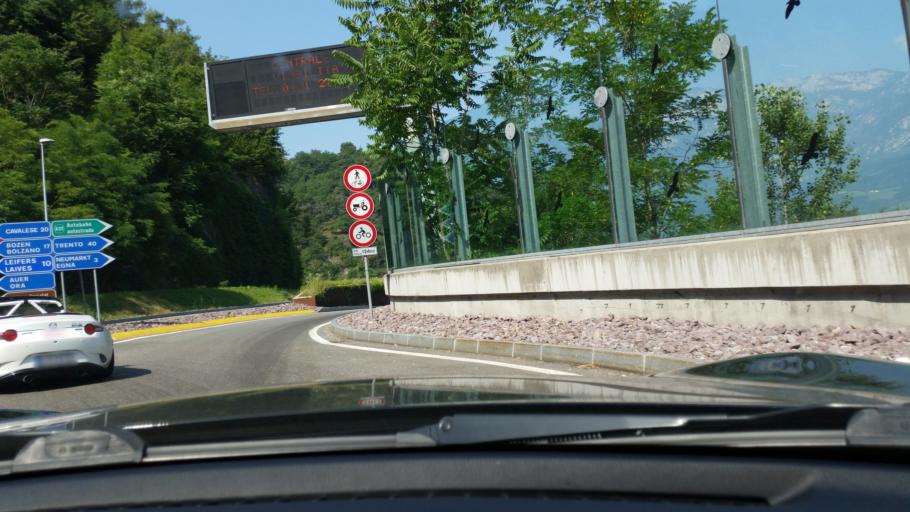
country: IT
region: Trentino-Alto Adige
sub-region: Bolzano
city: Ora
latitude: 46.3420
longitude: 11.2991
